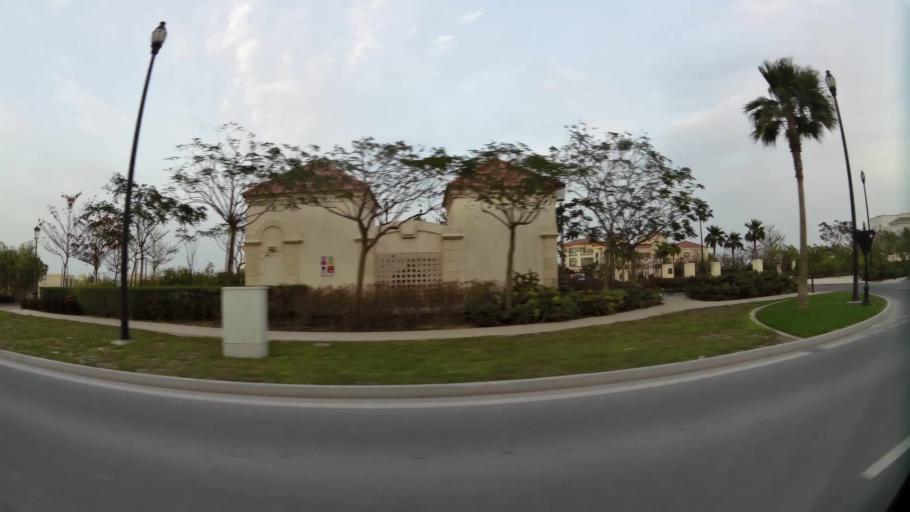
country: QA
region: Baladiyat ad Dawhah
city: Doha
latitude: 25.3642
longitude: 51.5644
